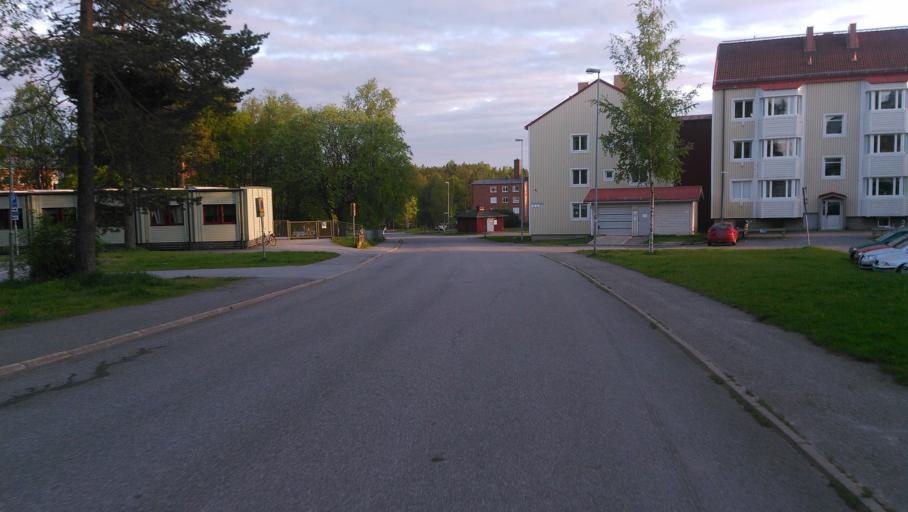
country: SE
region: Vaesterbotten
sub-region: Umea Kommun
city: Umea
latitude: 63.8259
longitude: 20.2999
